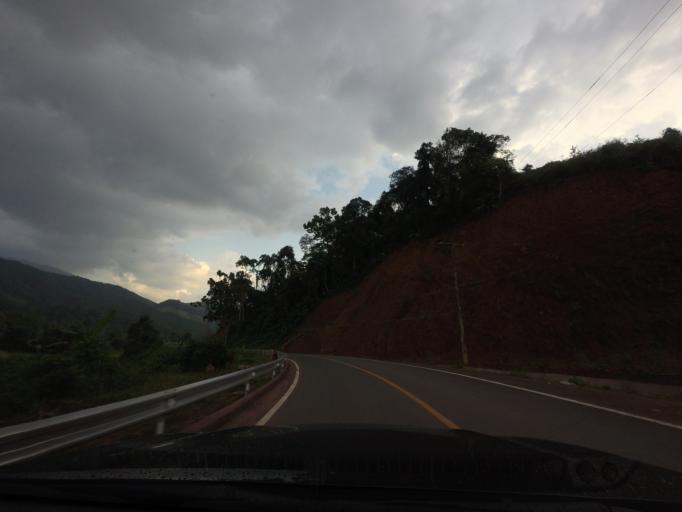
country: TH
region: Nan
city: Bo Kluea
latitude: 19.2227
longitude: 101.1824
